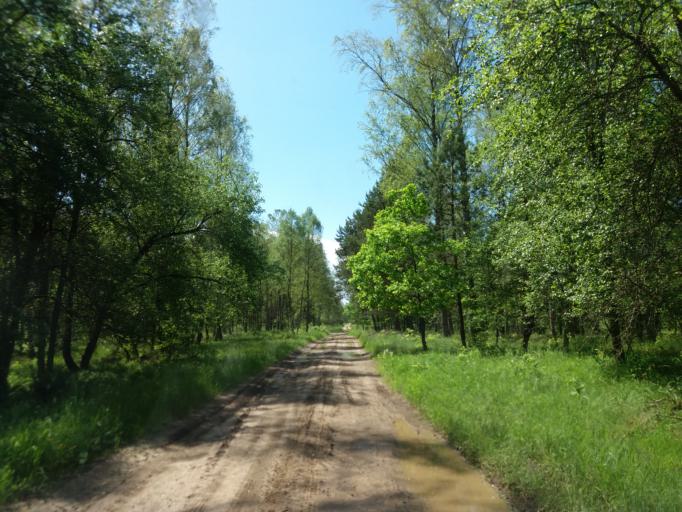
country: PL
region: West Pomeranian Voivodeship
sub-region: Powiat choszczenski
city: Drawno
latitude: 53.2638
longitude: 15.7395
